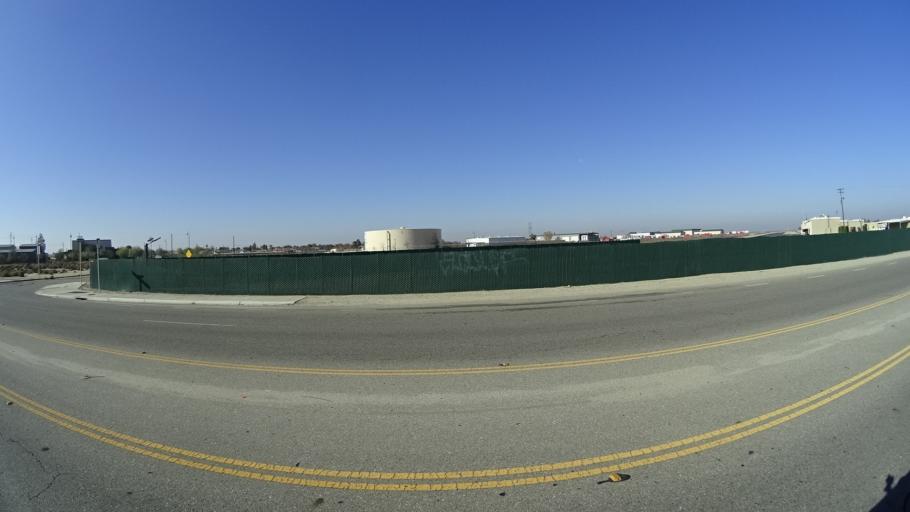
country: US
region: California
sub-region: Kern County
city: Rosedale
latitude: 35.4015
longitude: -119.1454
